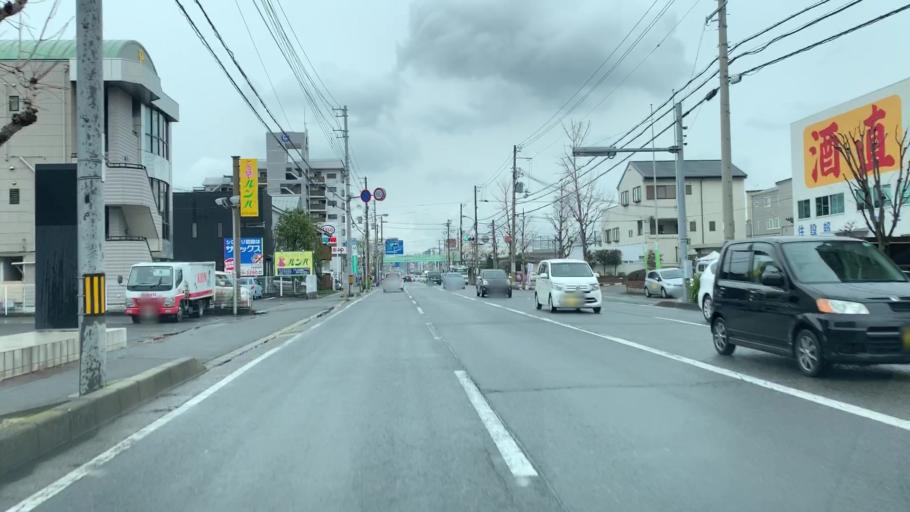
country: JP
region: Wakayama
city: Wakayama-shi
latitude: 34.2209
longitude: 135.1596
